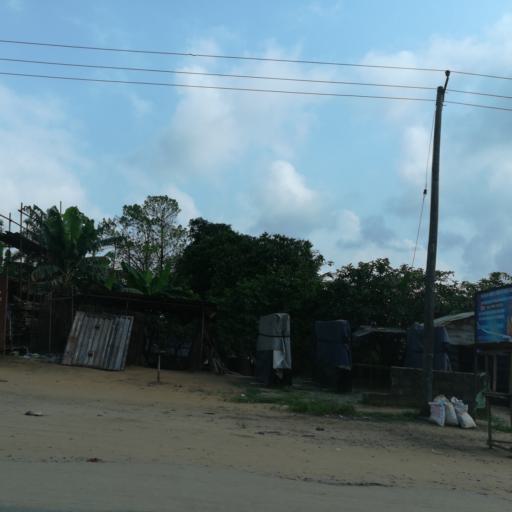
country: NG
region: Rivers
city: Okrika
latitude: 4.7796
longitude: 7.1259
